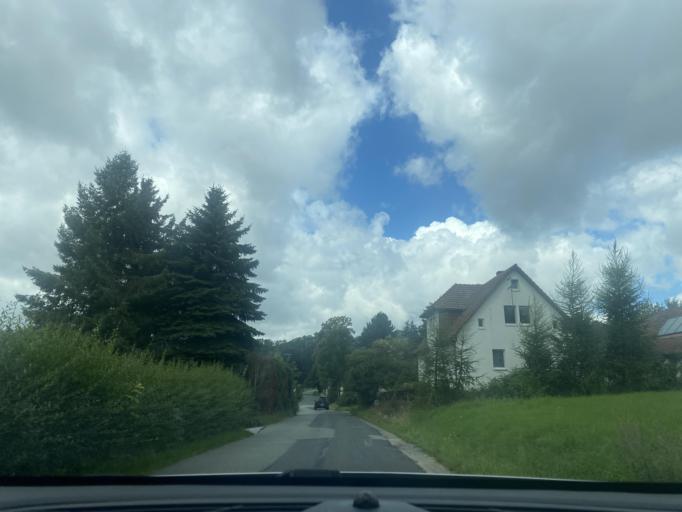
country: DE
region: Saxony
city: Sohland am Rotstein
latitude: 51.1289
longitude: 14.7837
